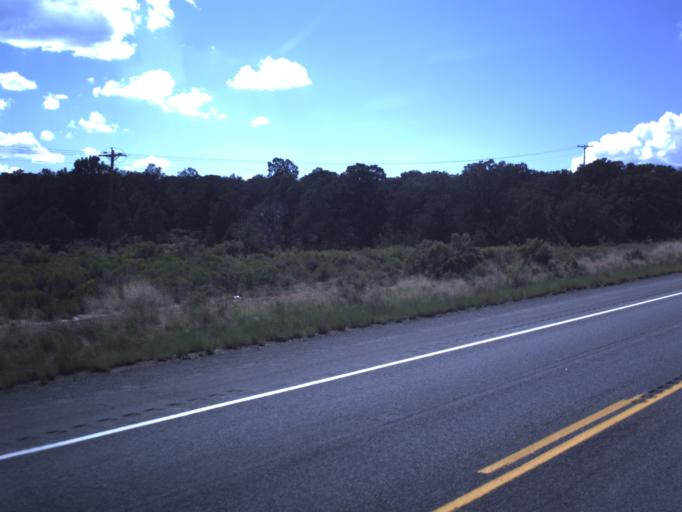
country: US
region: Utah
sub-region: Duchesne County
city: Duchesne
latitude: 40.1977
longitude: -110.6925
